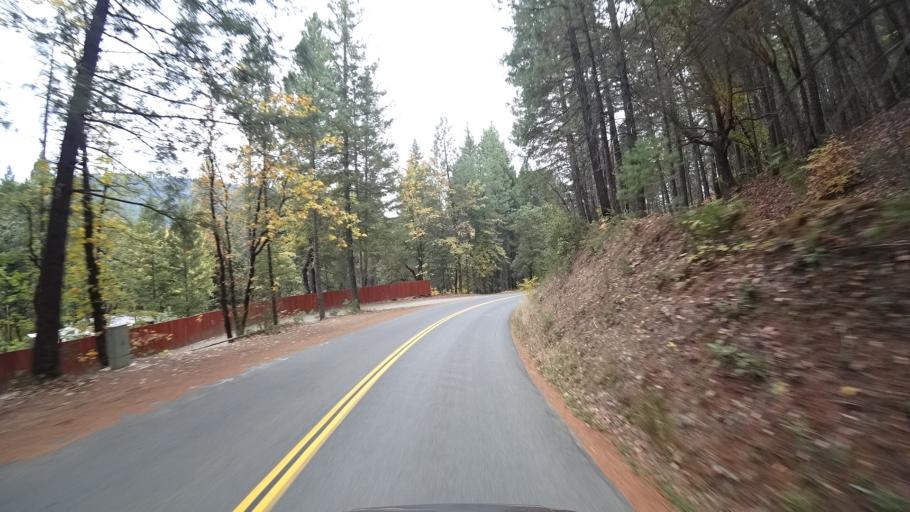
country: US
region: California
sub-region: Siskiyou County
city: Happy Camp
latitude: 41.7843
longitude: -123.3876
